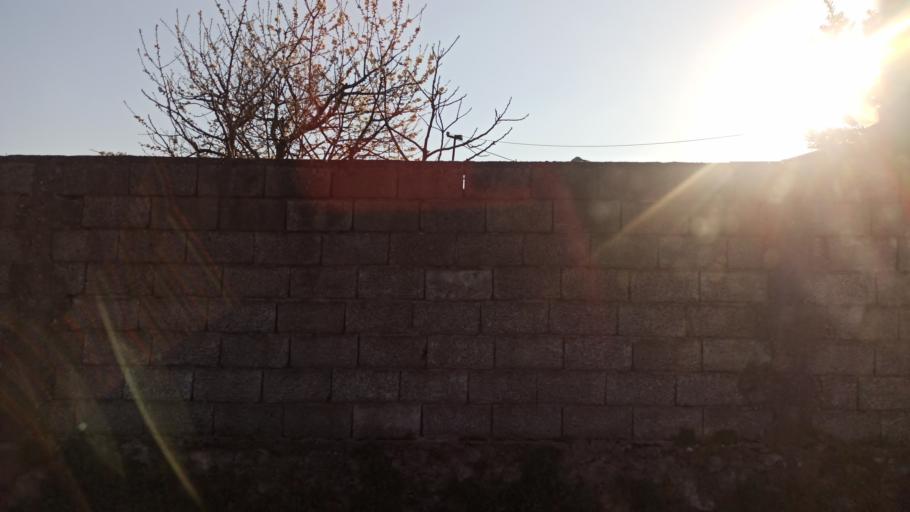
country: AL
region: Shkoder
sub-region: Rrethi i Shkodres
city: Shkoder
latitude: 42.0777
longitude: 19.5016
